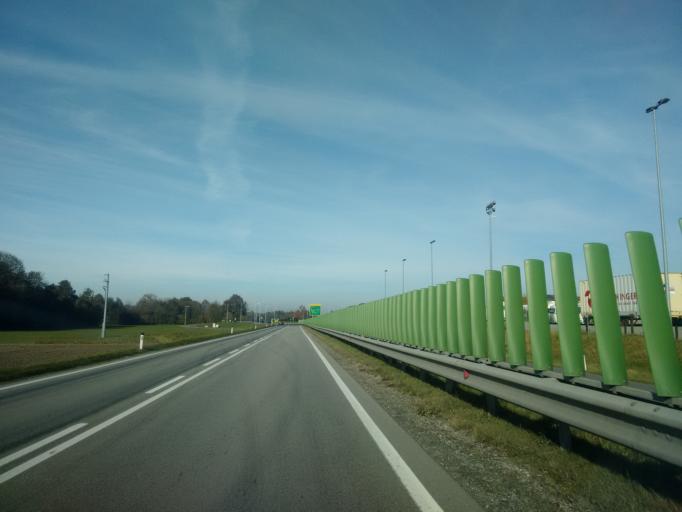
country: AT
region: Upper Austria
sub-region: Politischer Bezirk Ried im Innkreis
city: Ried im Innkreis
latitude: 48.2012
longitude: 13.5377
